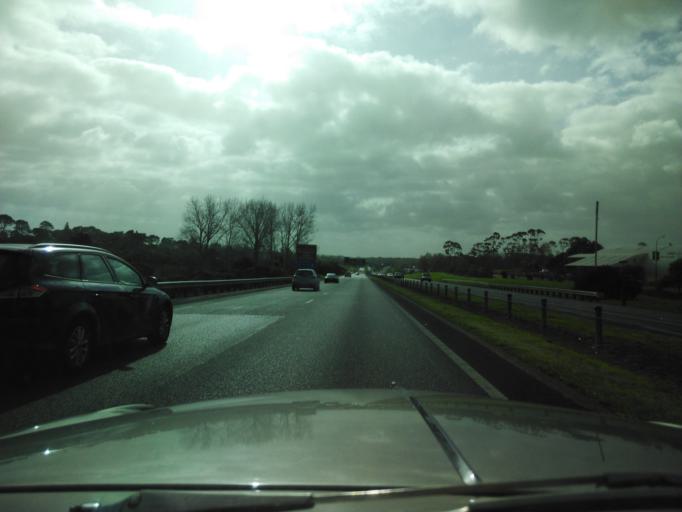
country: NZ
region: Auckland
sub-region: Auckland
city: Rothesay Bay
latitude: -36.6343
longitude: 174.6627
